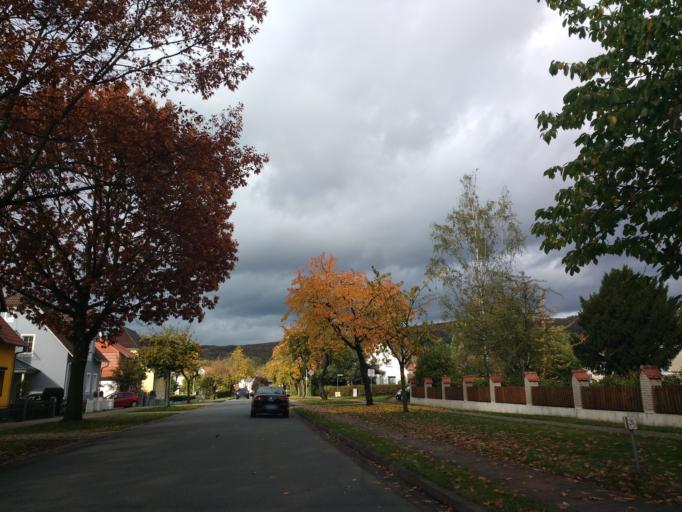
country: DE
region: Lower Saxony
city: Herzberg am Harz
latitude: 51.6577
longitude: 10.3508
